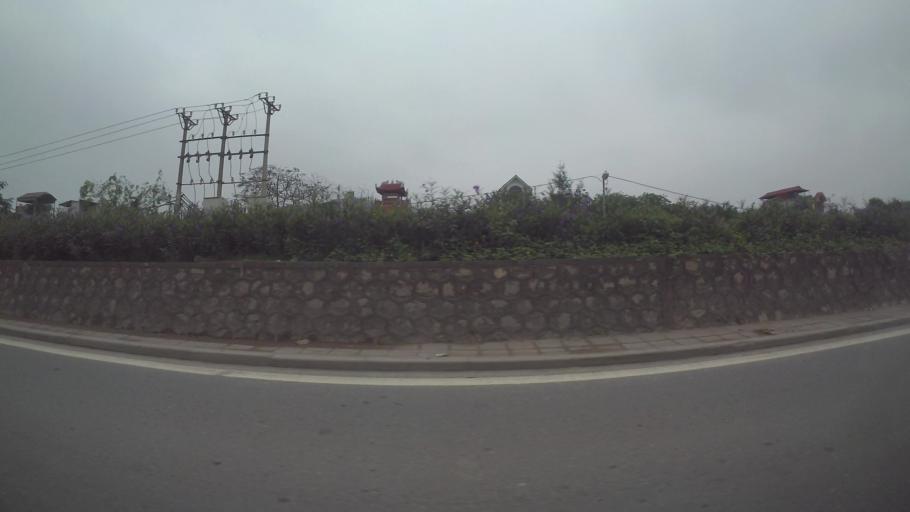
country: VN
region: Hung Yen
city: Van Giang
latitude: 20.9807
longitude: 105.8939
